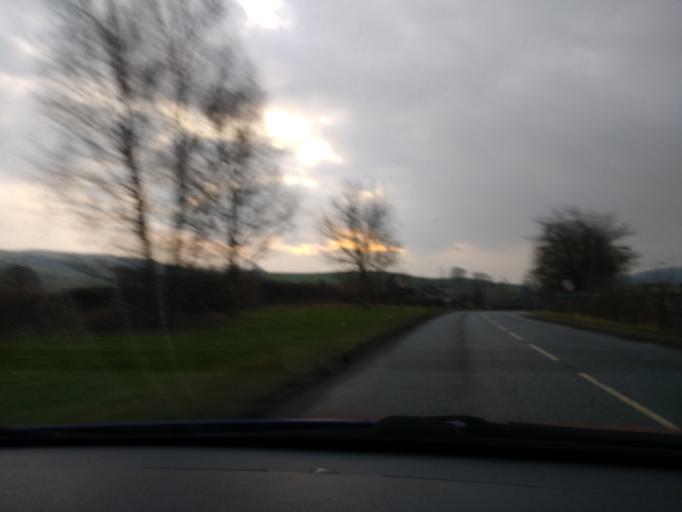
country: GB
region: England
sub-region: Cumbria
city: Milnthorpe
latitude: 54.2439
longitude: -2.7138
